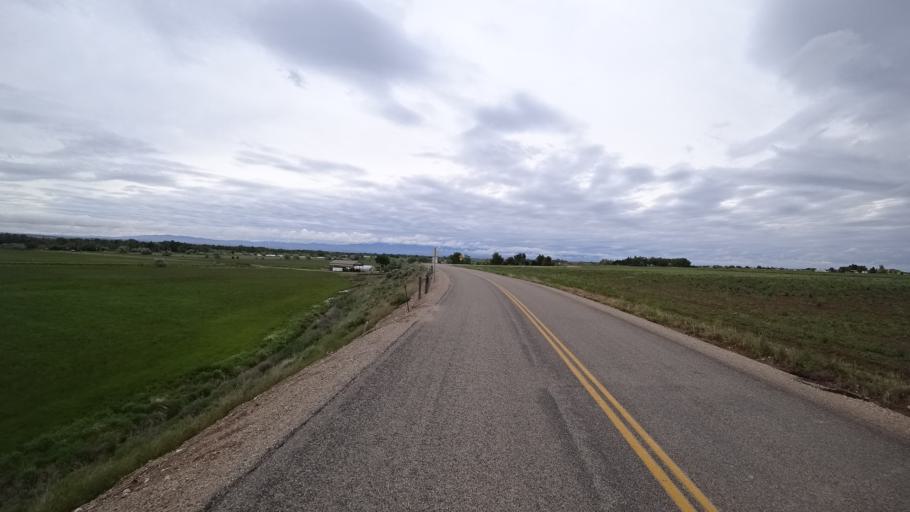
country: US
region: Idaho
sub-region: Ada County
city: Star
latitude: 43.6708
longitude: -116.5120
